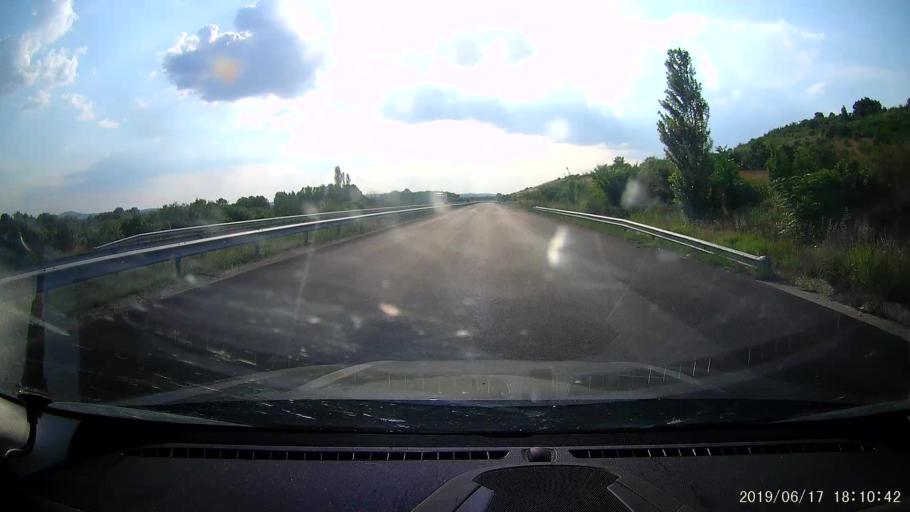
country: BG
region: Khaskovo
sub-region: Obshtina Lyubimets
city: Lyubimets
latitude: 41.8766
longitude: 26.0705
